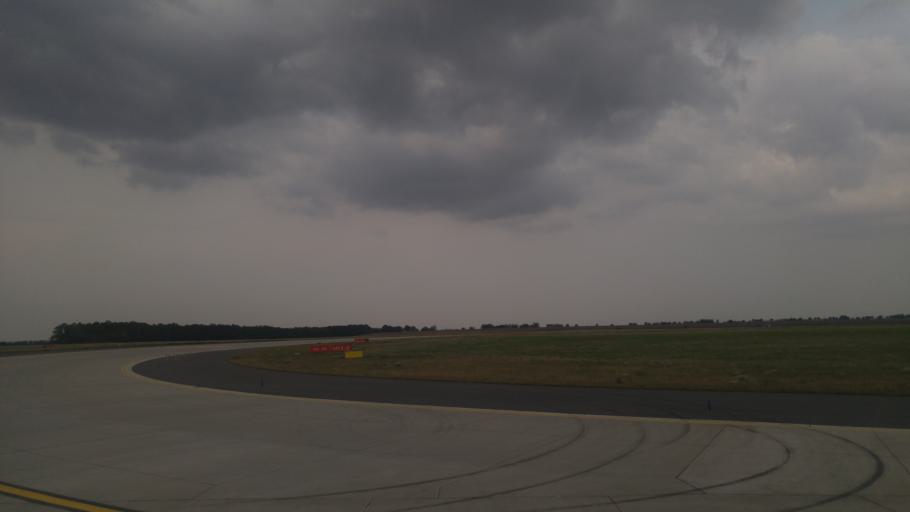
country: CZ
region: Central Bohemia
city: Jenec
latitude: 50.1022
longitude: 14.2354
